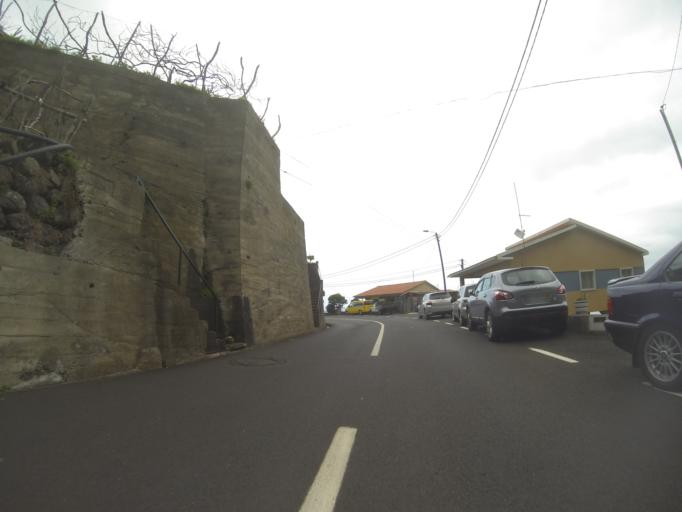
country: PT
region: Madeira
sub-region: Porto Moniz
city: Porto Moniz
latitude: 32.8221
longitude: -17.1063
